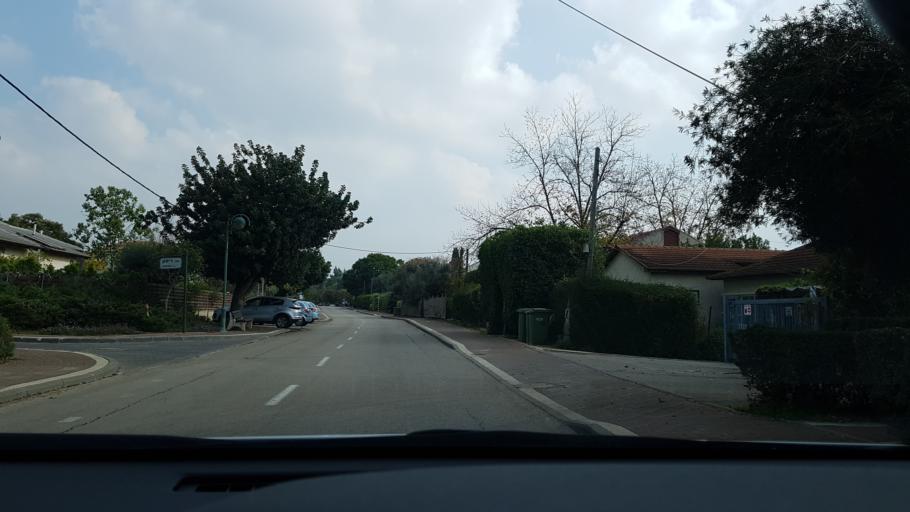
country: IL
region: Central District
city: Mazkeret Batya
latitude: 31.8704
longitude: 34.8235
